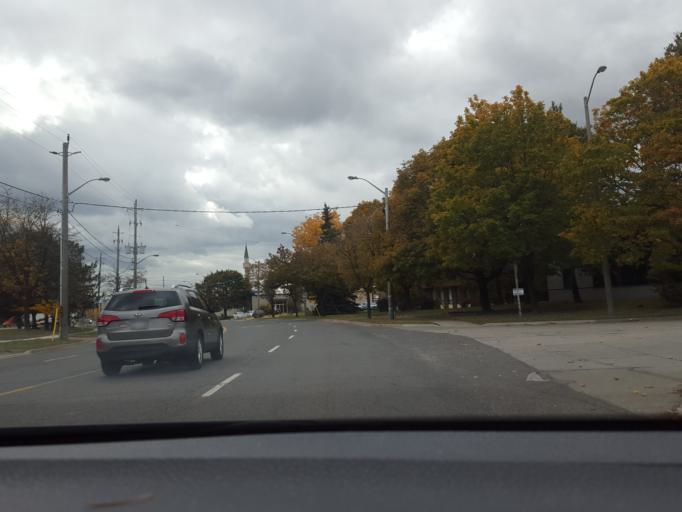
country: CA
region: Ontario
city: Etobicoke
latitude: 43.6224
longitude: -79.5500
